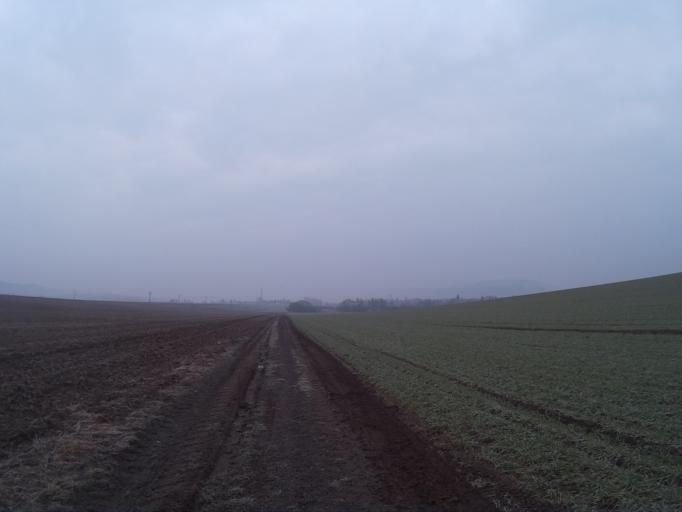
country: HU
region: Komarom-Esztergom
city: Tarjan
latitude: 47.6228
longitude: 18.5032
